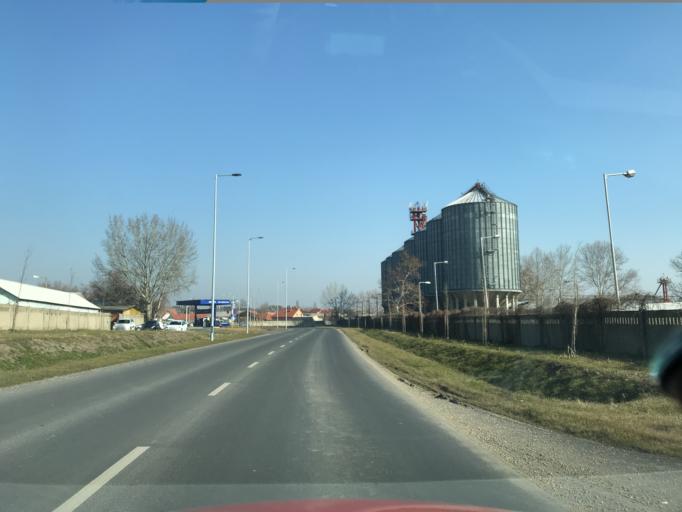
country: HU
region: Gyor-Moson-Sopron
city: Gyor
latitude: 47.6786
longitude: 17.6090
